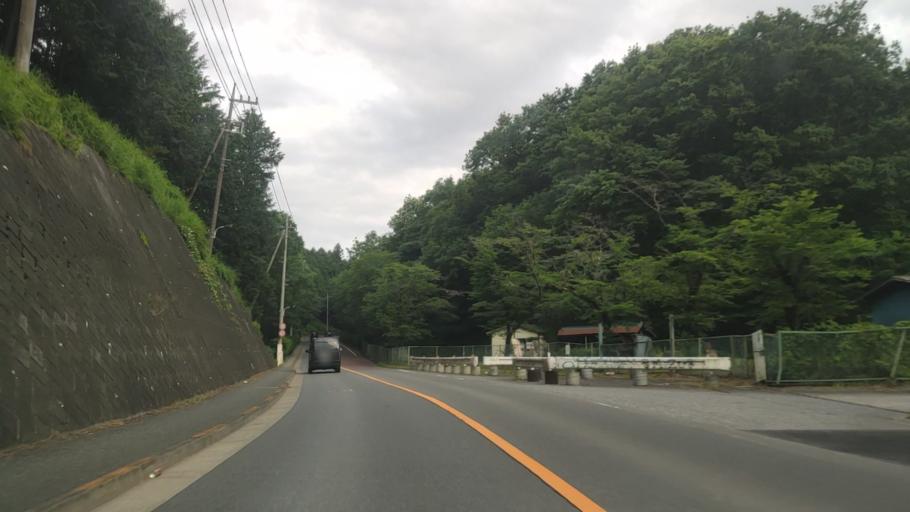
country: JP
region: Saitama
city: Hanno
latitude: 35.8132
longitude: 139.2986
